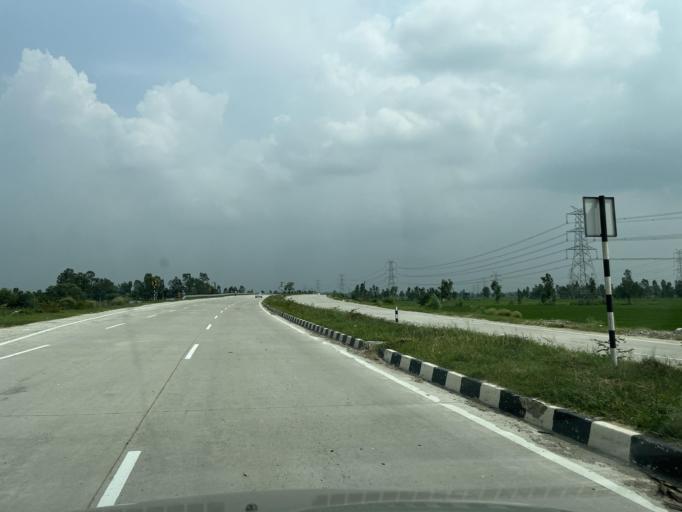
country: IN
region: Uttarakhand
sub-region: Udham Singh Nagar
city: Jaspur
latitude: 29.2904
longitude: 78.8511
